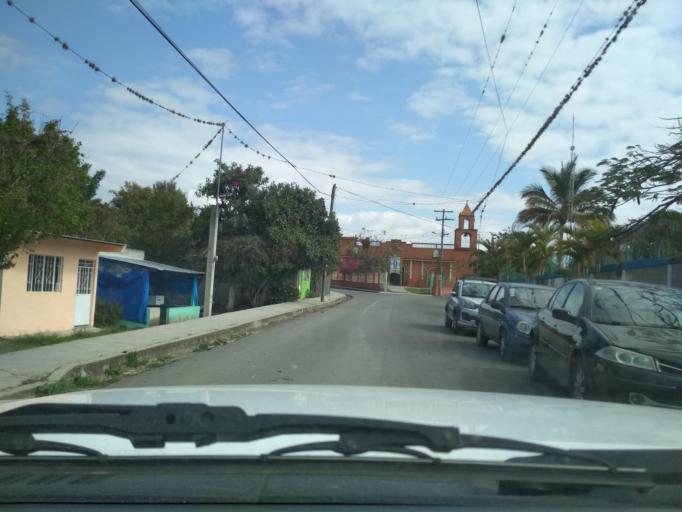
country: MX
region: Veracruz
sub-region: Coatepec
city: Tuzamapan
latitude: 19.3706
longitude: -96.8814
